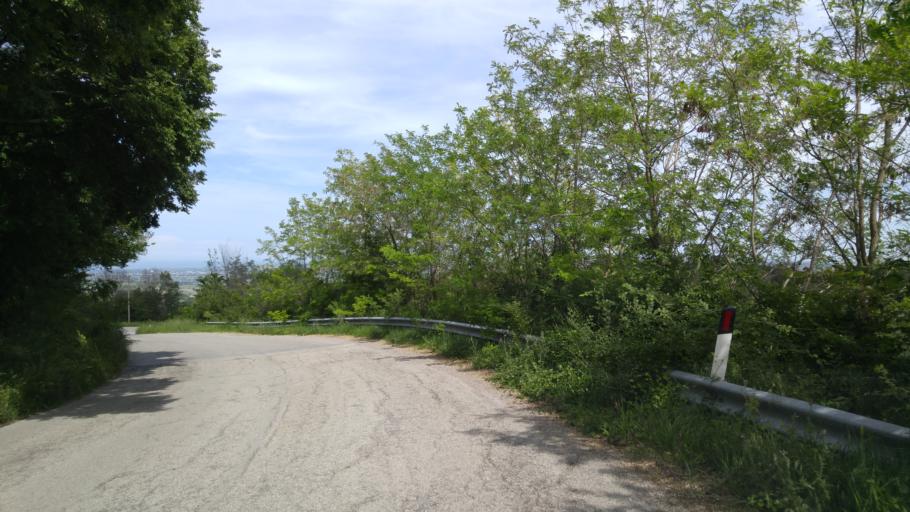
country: IT
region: The Marches
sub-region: Provincia di Pesaro e Urbino
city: Cartoceto
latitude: 43.7684
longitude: 12.8654
